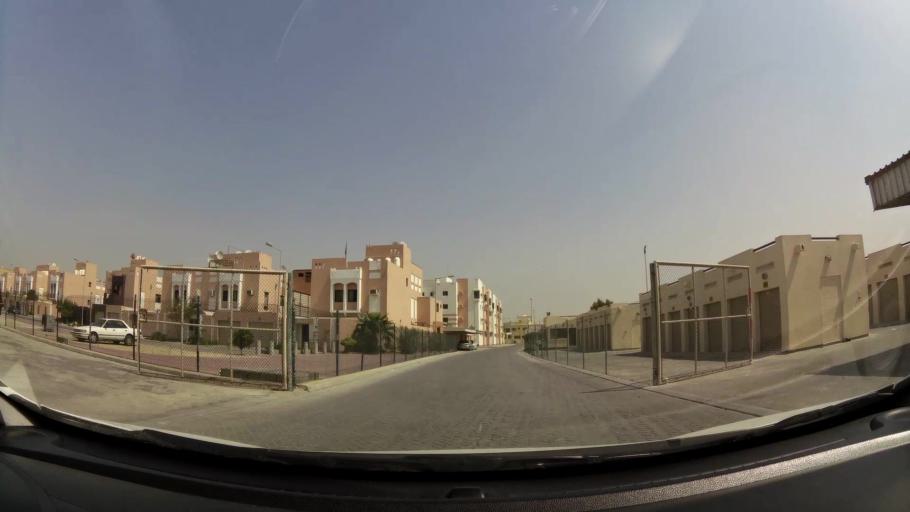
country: BH
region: Manama
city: Jidd Hafs
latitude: 26.2150
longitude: 50.4446
